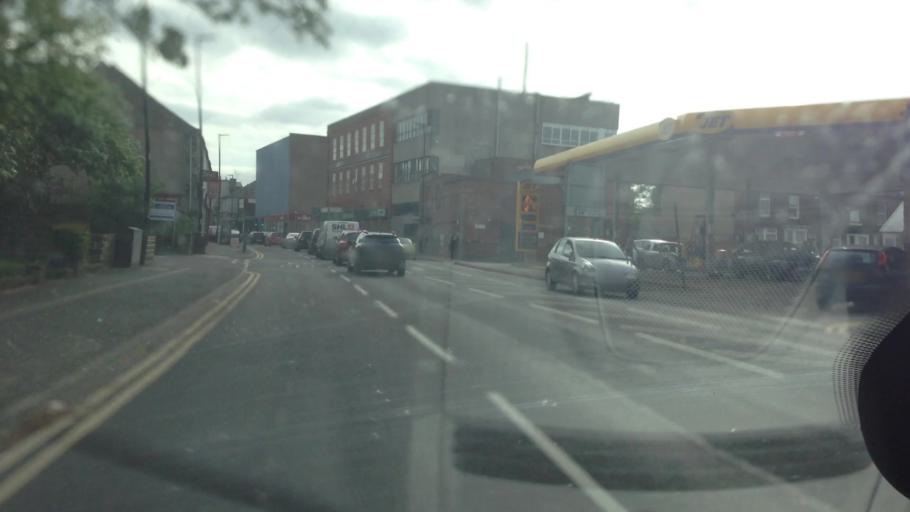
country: GB
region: England
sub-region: Sheffield
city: Sheffield
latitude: 53.4038
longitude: -1.4989
